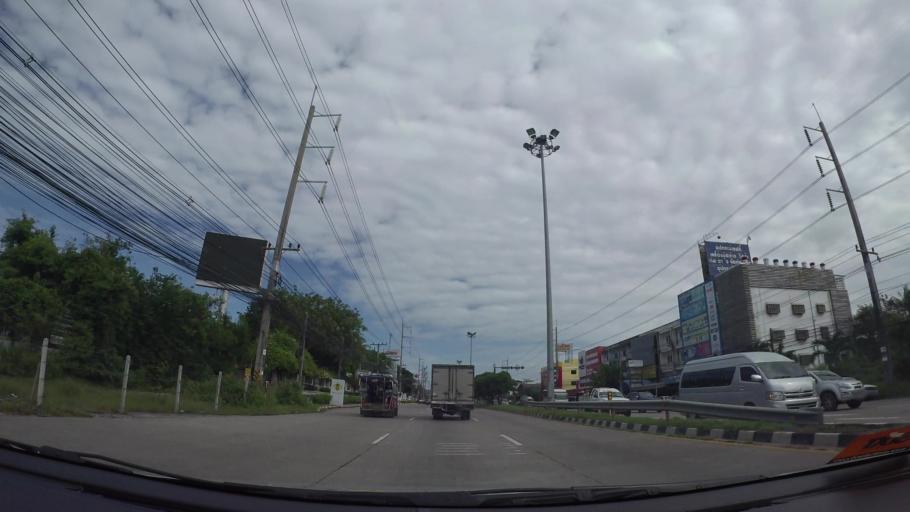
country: TH
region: Rayong
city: Ban Chang
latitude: 12.7216
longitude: 101.1541
